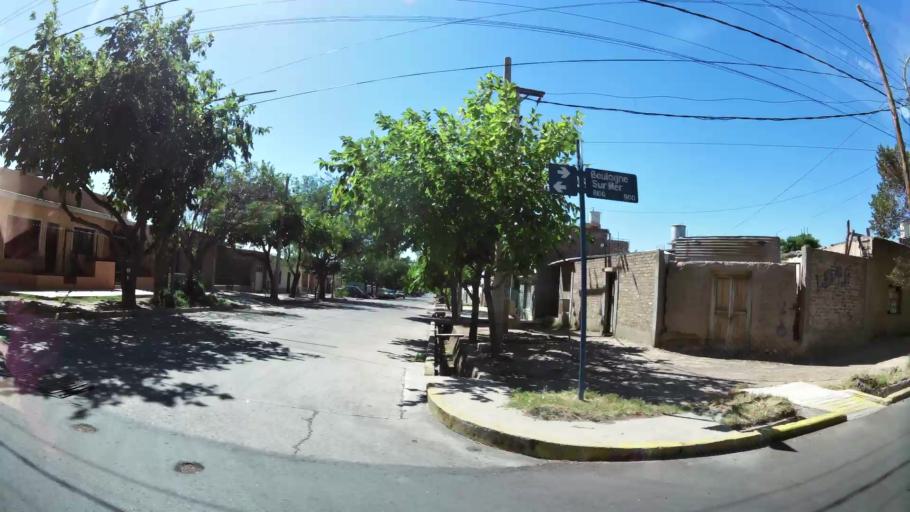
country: AR
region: Mendoza
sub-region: Departamento de Godoy Cruz
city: Godoy Cruz
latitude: -32.9175
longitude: -68.8637
